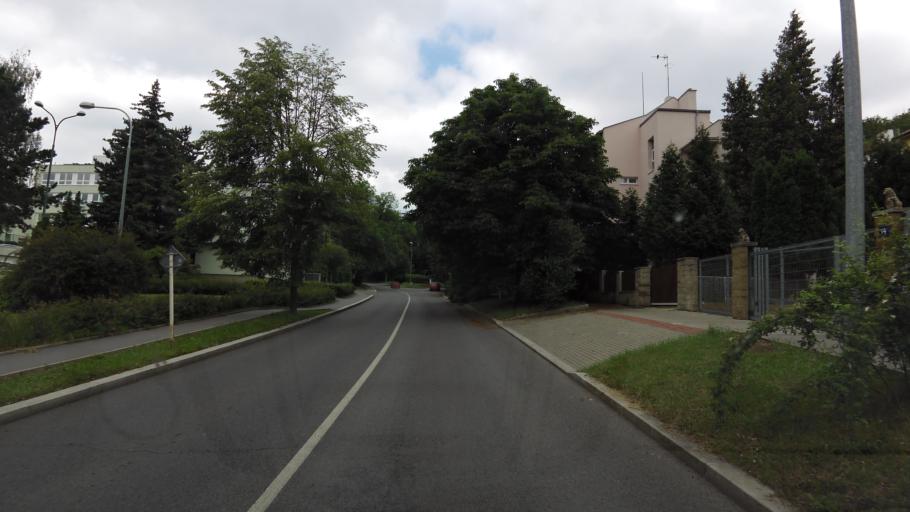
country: CZ
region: Praha
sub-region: Praha 1
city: Mala Strana
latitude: 50.0711
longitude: 14.3610
